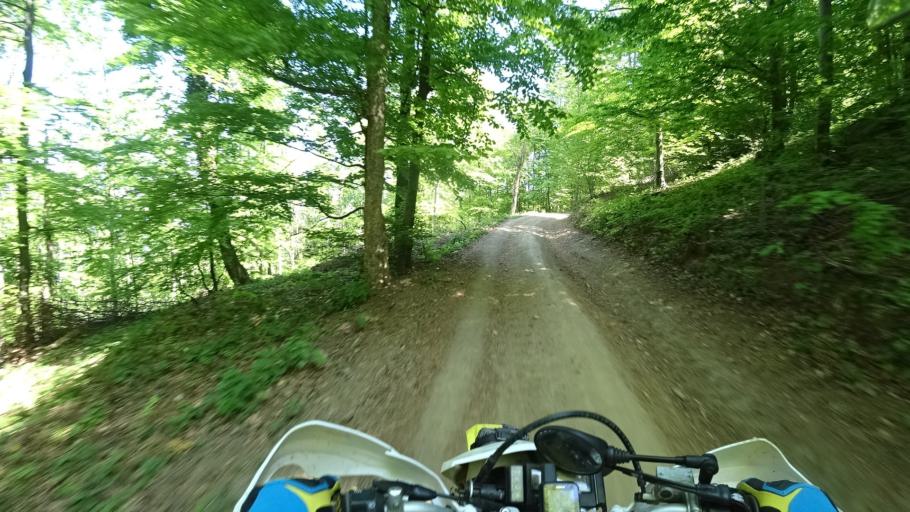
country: HR
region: Zagrebacka
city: Jablanovec
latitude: 45.8683
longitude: 15.8620
